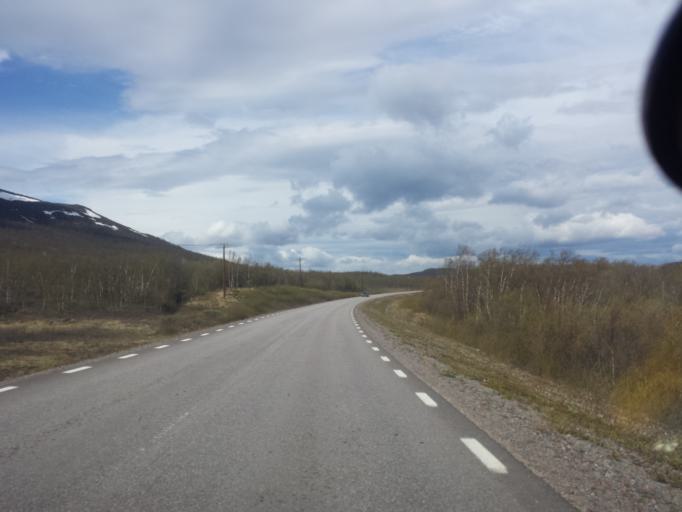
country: SE
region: Norrbotten
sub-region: Kiruna Kommun
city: Kiruna
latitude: 68.1625
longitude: 19.7800
